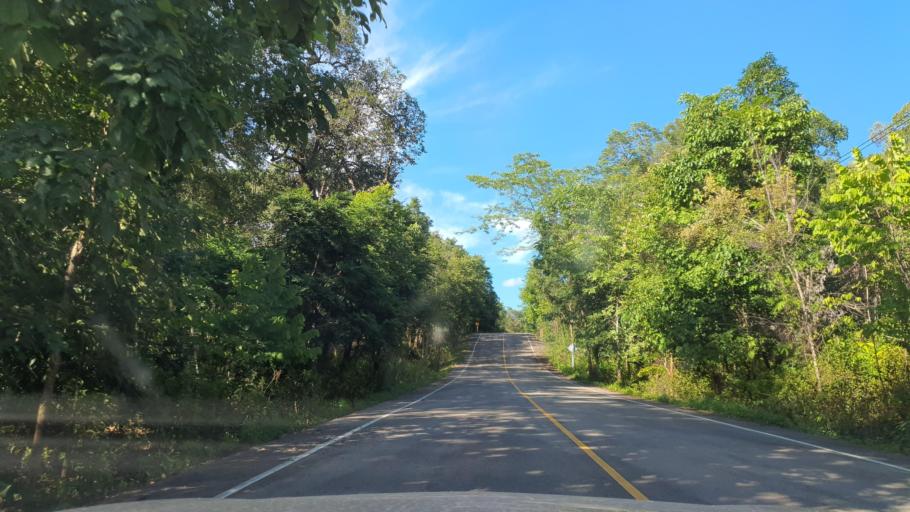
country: TH
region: Chiang Mai
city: Mae On
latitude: 18.7885
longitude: 99.3002
